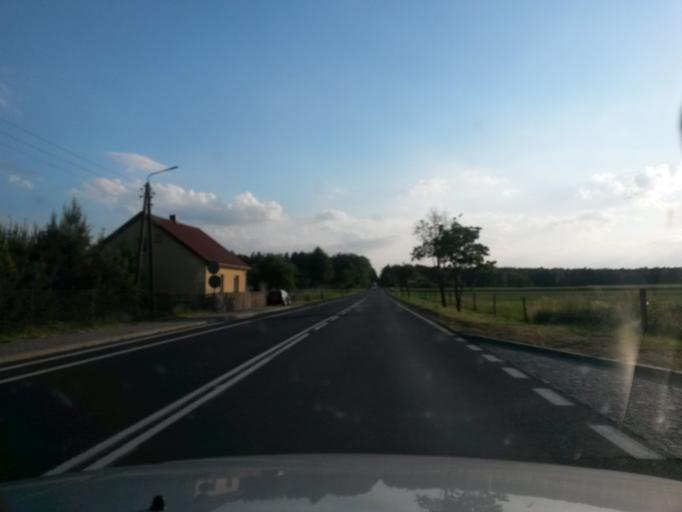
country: PL
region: Lodz Voivodeship
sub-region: Powiat wielunski
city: Osjakow
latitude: 51.2601
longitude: 18.7444
